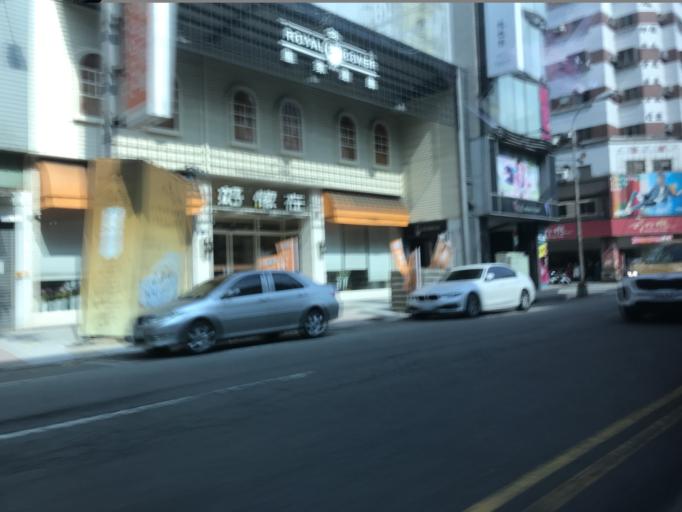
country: TW
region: Taiwan
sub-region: Taichung City
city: Taichung
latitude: 24.1468
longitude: 120.6546
